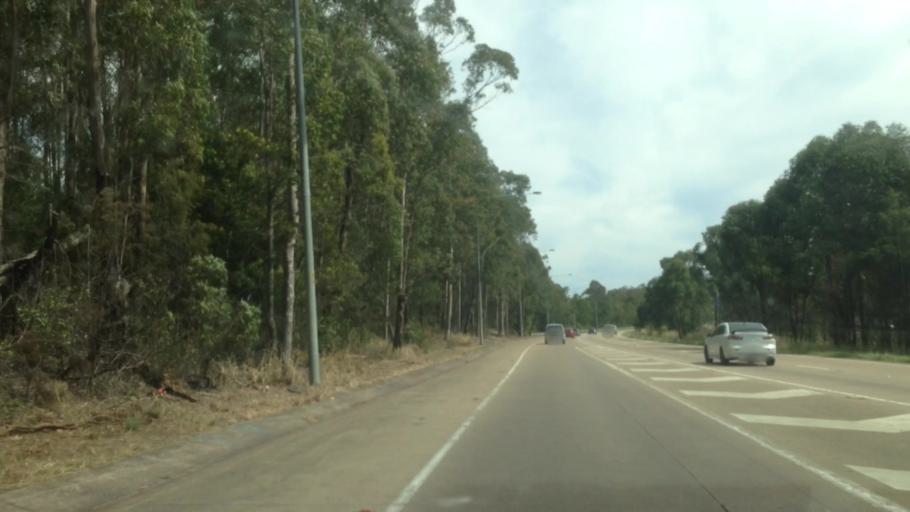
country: AU
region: New South Wales
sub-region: Lake Macquarie Shire
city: Holmesville
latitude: -32.8927
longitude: 151.5970
